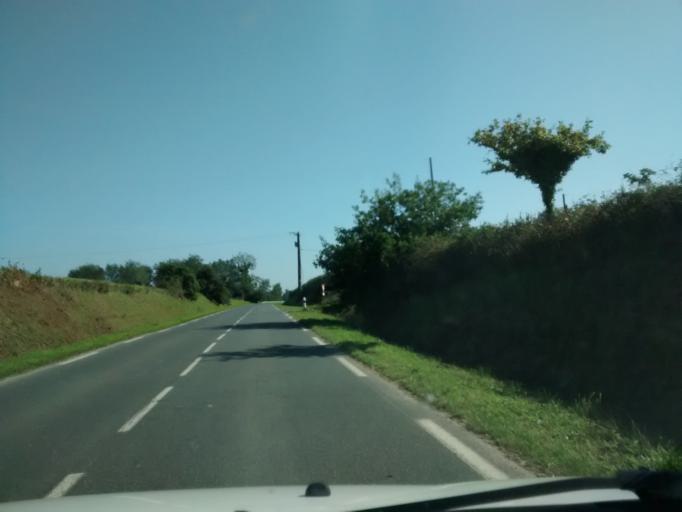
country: FR
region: Brittany
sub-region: Departement des Cotes-d'Armor
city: Pleumeur-Gautier
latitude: 48.8288
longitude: -3.1664
